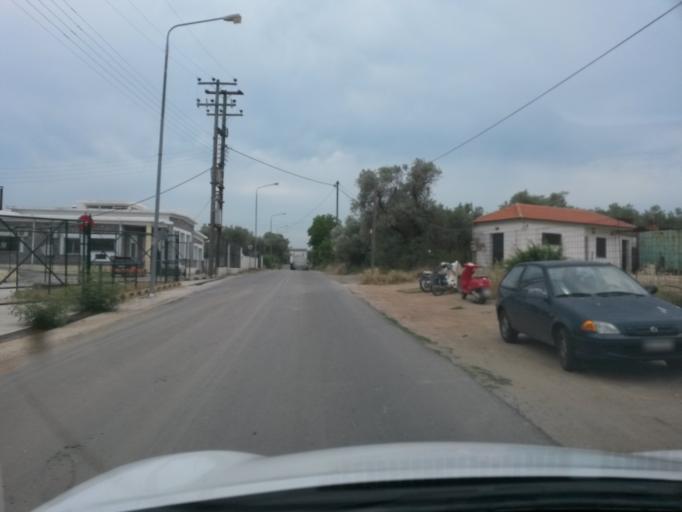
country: GR
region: North Aegean
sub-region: Nomos Lesvou
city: Palaiokipos
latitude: 39.0518
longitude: 26.4547
